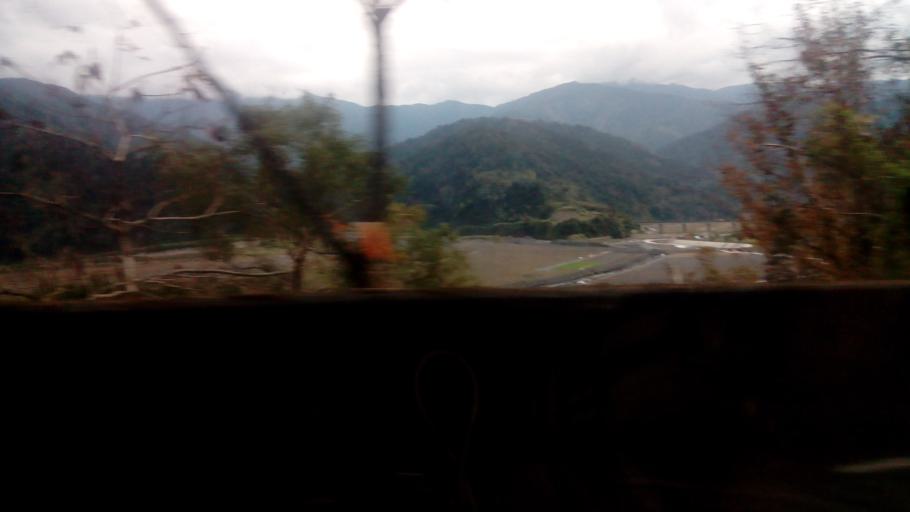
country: TW
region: Taiwan
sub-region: Yilan
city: Yilan
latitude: 24.5816
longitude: 121.4951
